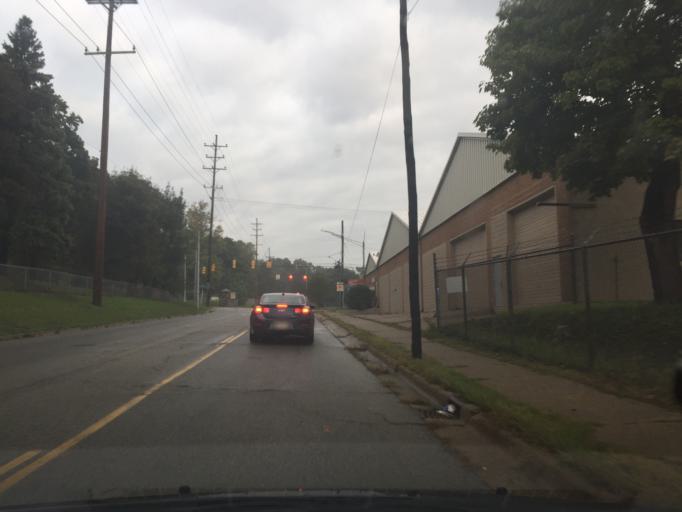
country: US
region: Michigan
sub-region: Oakland County
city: Pontiac
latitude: 42.6423
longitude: -83.2827
